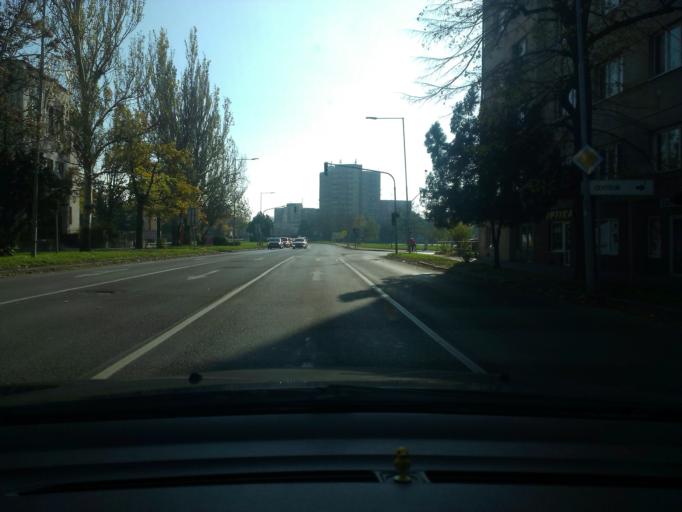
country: SK
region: Nitriansky
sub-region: Okres Nove Zamky
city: Nove Zamky
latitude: 47.9889
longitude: 18.1710
